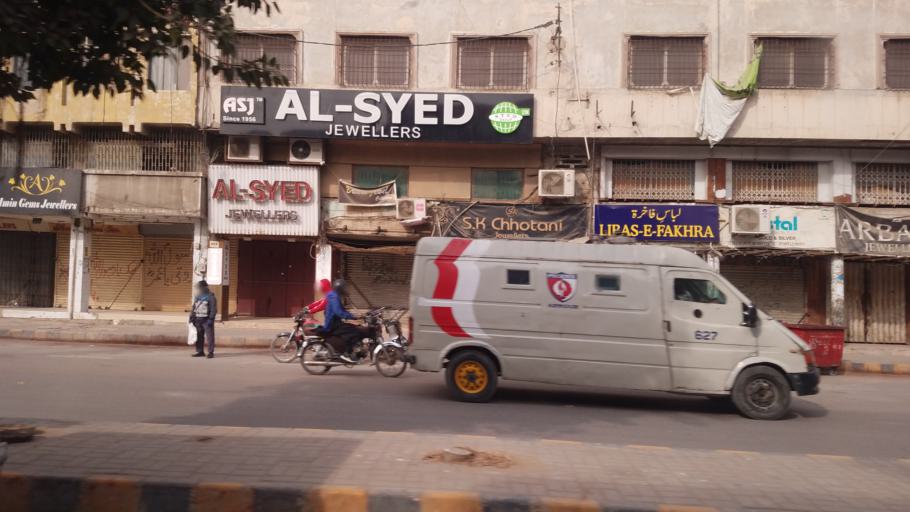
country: PK
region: Sindh
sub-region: Karachi District
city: Karachi
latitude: 24.8721
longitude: 67.0601
